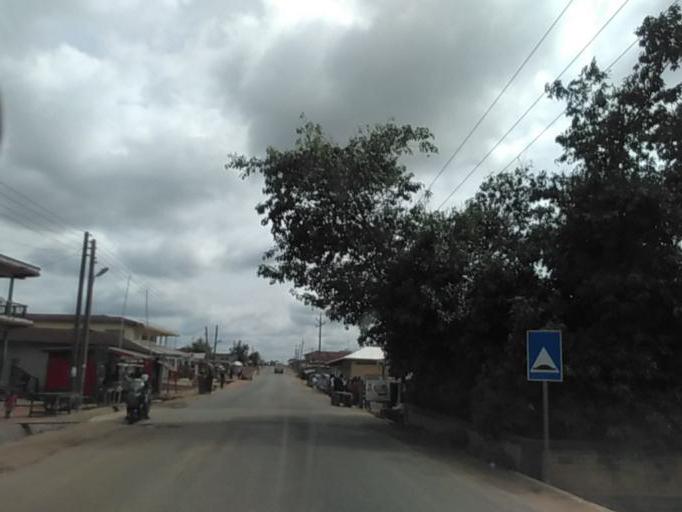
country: GH
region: Ashanti
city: Mamponteng
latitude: 6.7323
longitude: -1.4604
